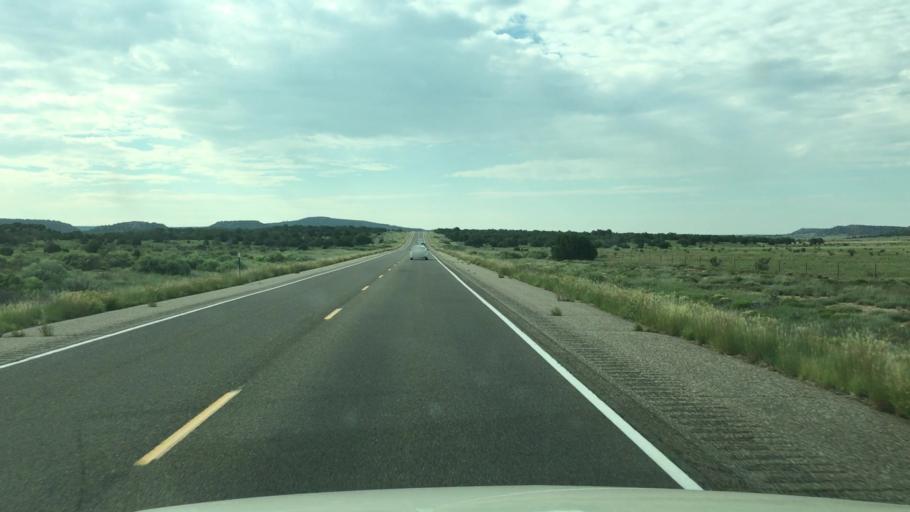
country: US
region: New Mexico
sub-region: Santa Fe County
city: Eldorado at Santa Fe
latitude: 35.3404
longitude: -105.8401
